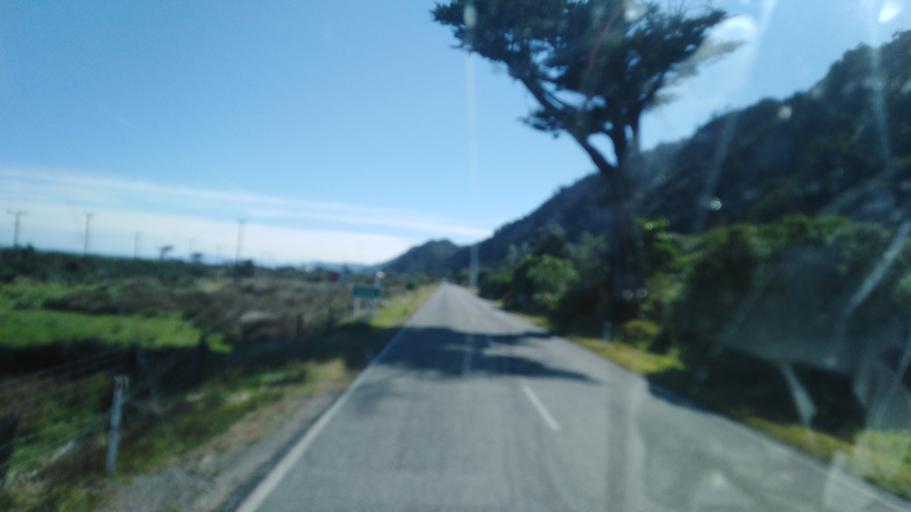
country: NZ
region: West Coast
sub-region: Buller District
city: Westport
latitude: -41.6410
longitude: 171.8431
